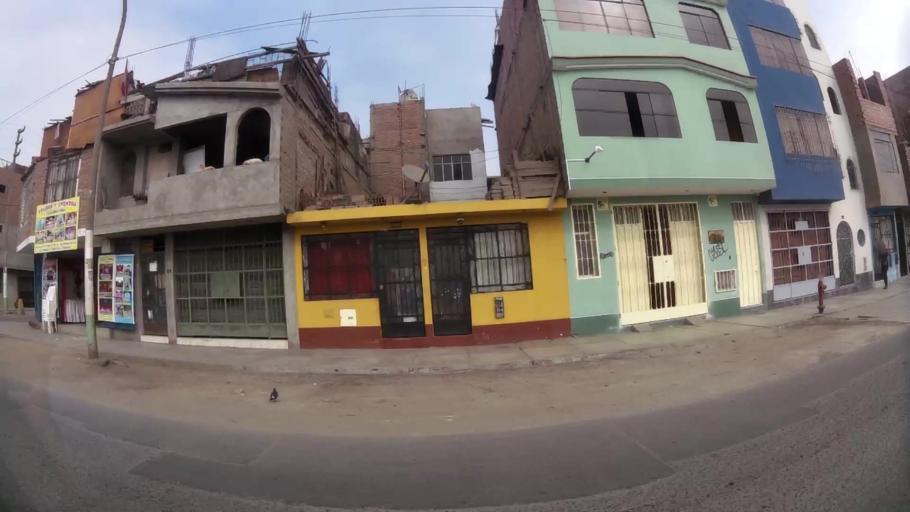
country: PE
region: Callao
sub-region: Callao
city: Callao
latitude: -12.0239
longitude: -77.0929
